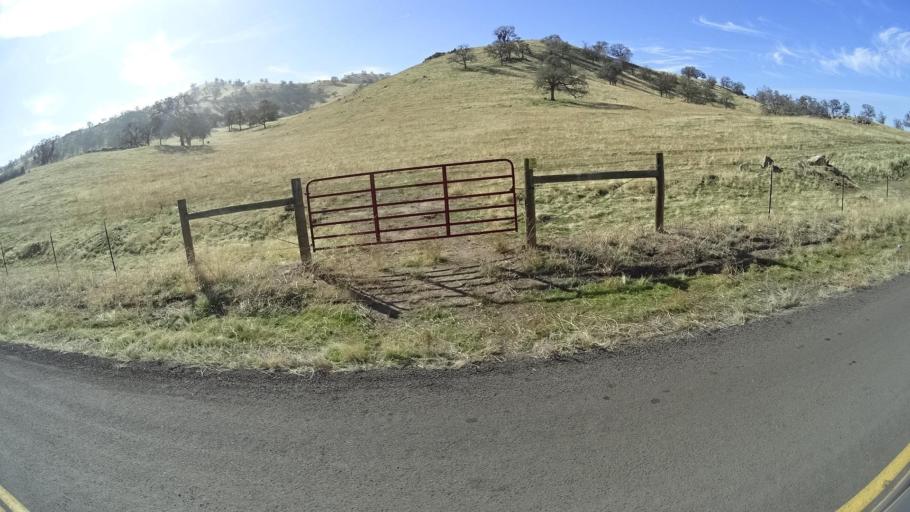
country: US
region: California
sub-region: Tulare County
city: Richgrove
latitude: 35.6970
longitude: -118.8389
